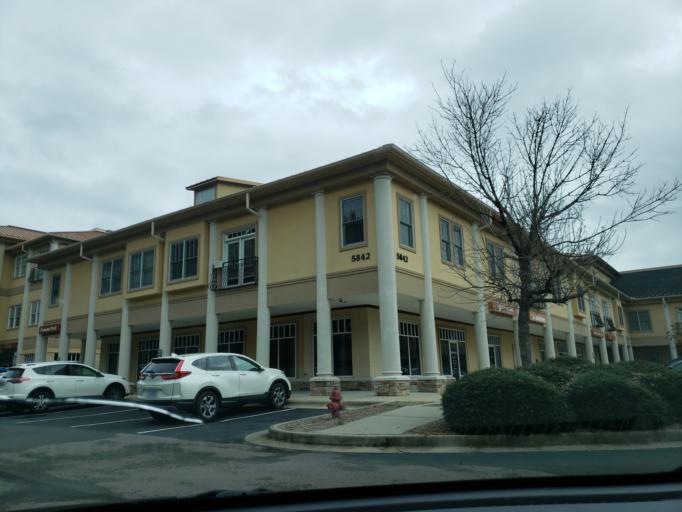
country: US
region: North Carolina
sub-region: Durham County
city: Durham
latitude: 35.9205
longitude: -78.9313
